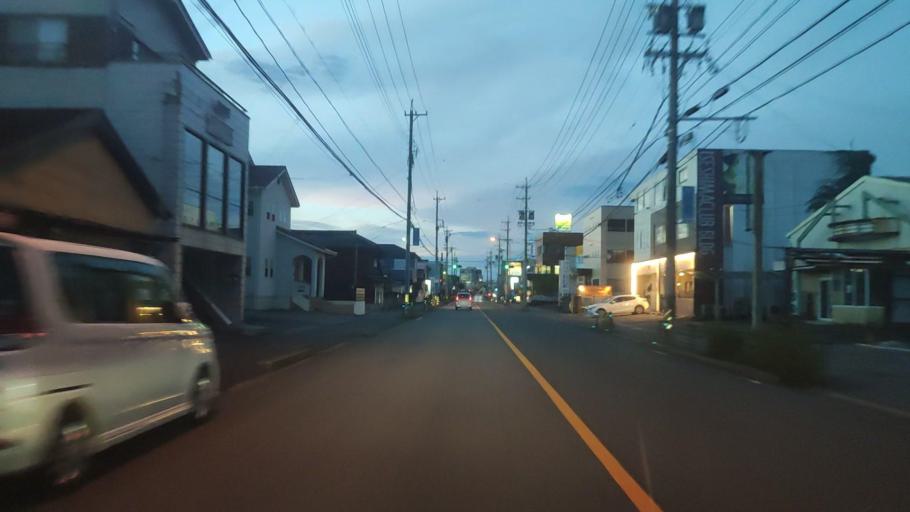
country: JP
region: Mie
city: Ise
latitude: 34.5010
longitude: 136.7162
